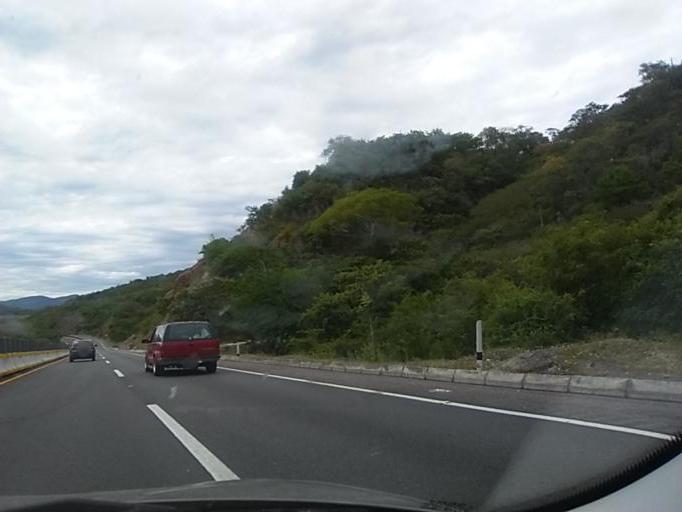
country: MX
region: Guerrero
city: Copalillo
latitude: 18.1308
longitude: -99.2085
